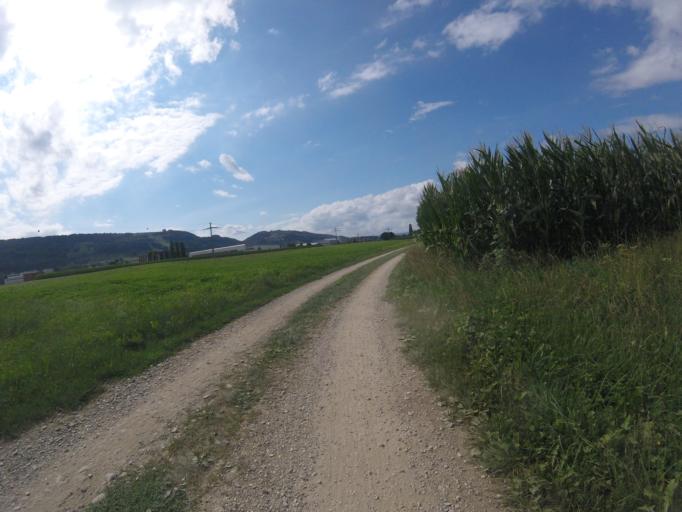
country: CH
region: Bern
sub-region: Bern-Mittelland District
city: Belp
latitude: 46.9022
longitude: 7.5105
